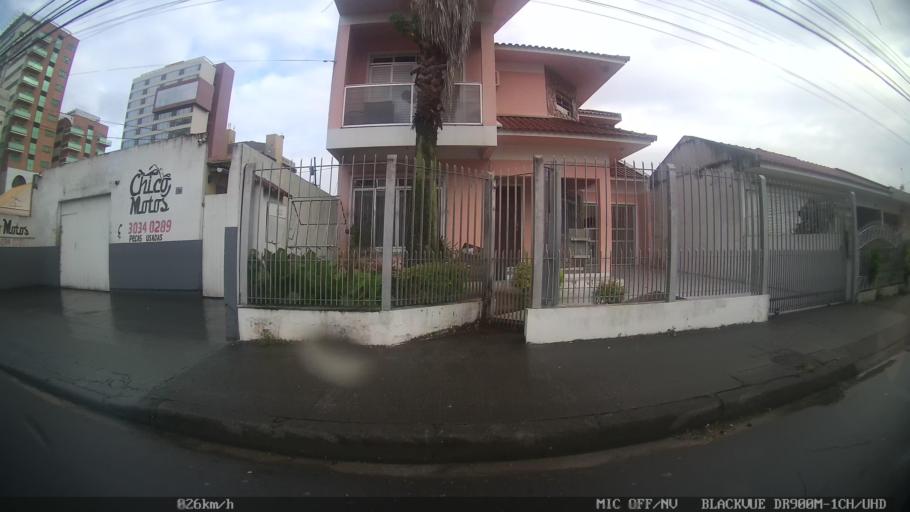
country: BR
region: Santa Catarina
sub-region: Sao Jose
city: Campinas
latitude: -27.5863
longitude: -48.6104
